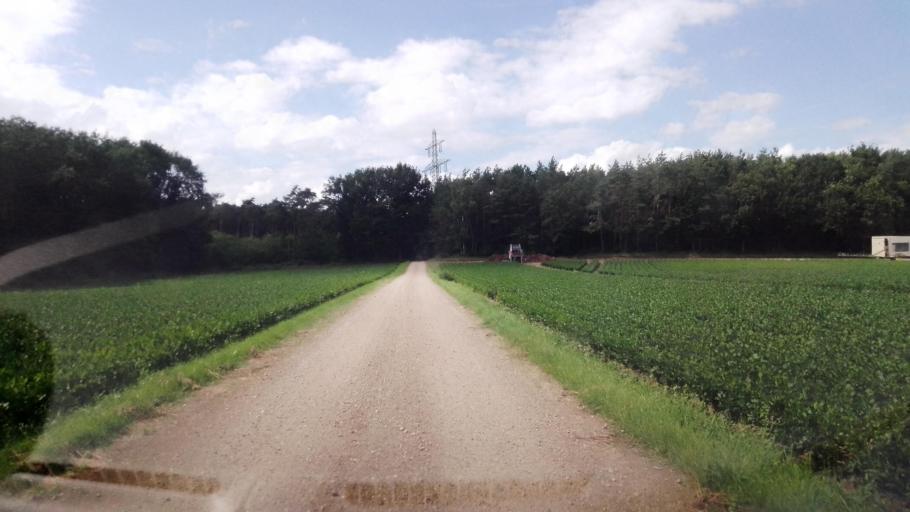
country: NL
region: Limburg
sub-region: Gemeente Venlo
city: Tegelen
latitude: 51.3532
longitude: 6.1105
